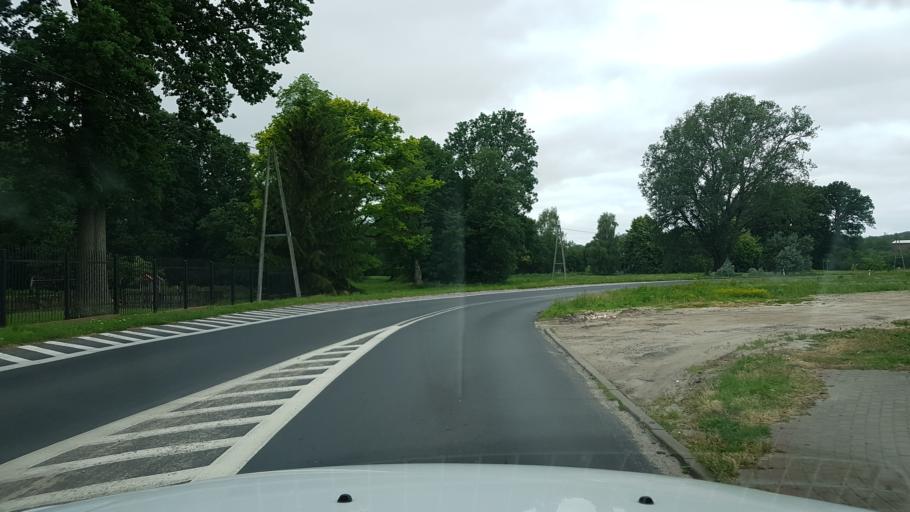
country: PL
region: West Pomeranian Voivodeship
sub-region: Powiat kamienski
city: Swierzno
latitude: 53.9498
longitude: 15.0071
